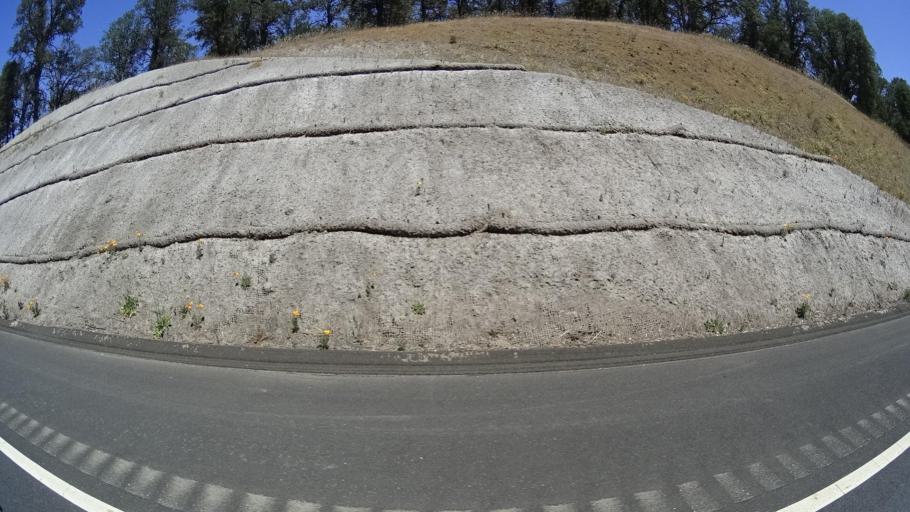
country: US
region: California
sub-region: Lake County
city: Lower Lake
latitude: 38.8998
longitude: -122.6104
